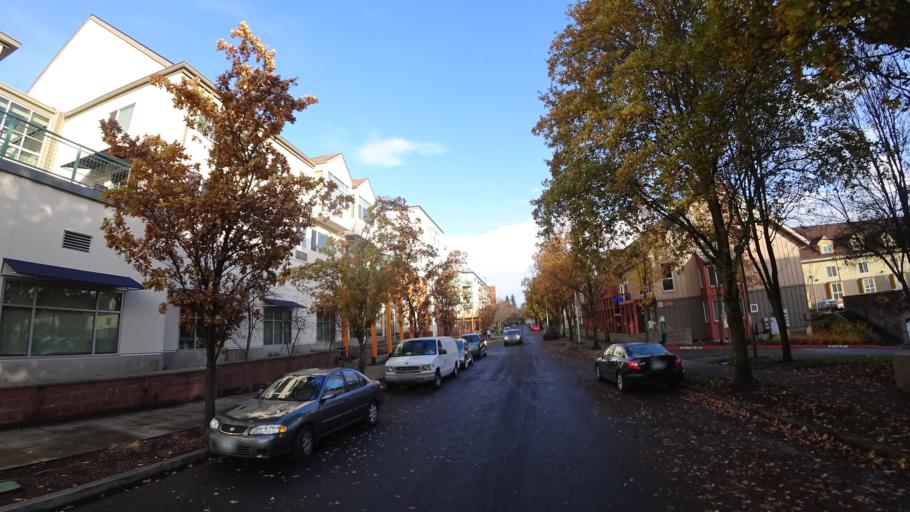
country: US
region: Oregon
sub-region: Multnomah County
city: Lents
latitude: 45.5217
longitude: -122.5580
